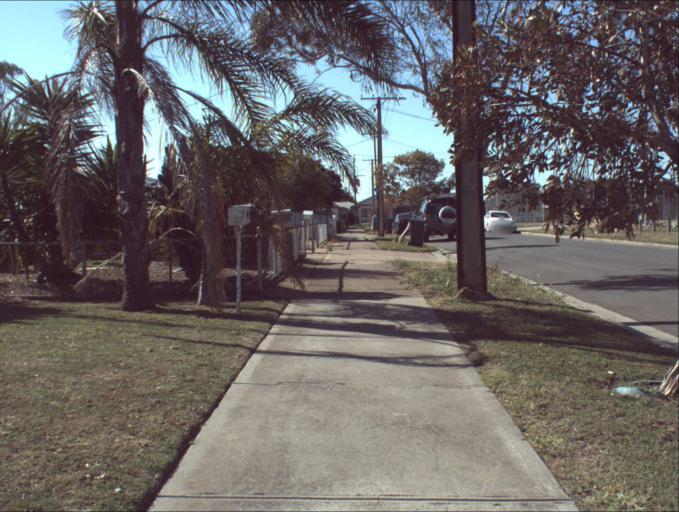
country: AU
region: South Australia
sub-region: Port Adelaide Enfield
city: Birkenhead
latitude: -34.8100
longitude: 138.5052
